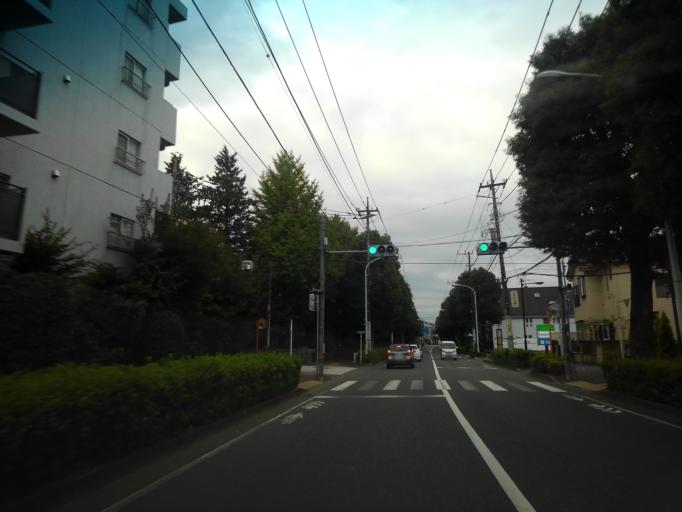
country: JP
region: Tokyo
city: Chofugaoka
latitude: 35.6590
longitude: 139.5406
